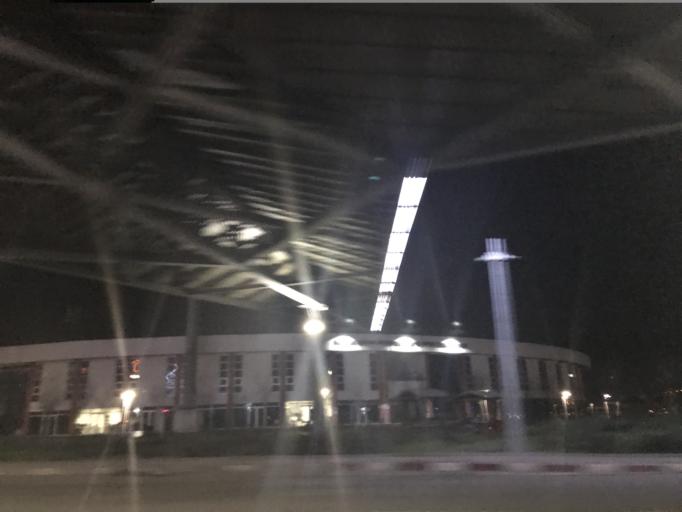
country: TR
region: Karabuk
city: Karabuk
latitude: 41.2064
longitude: 32.6581
